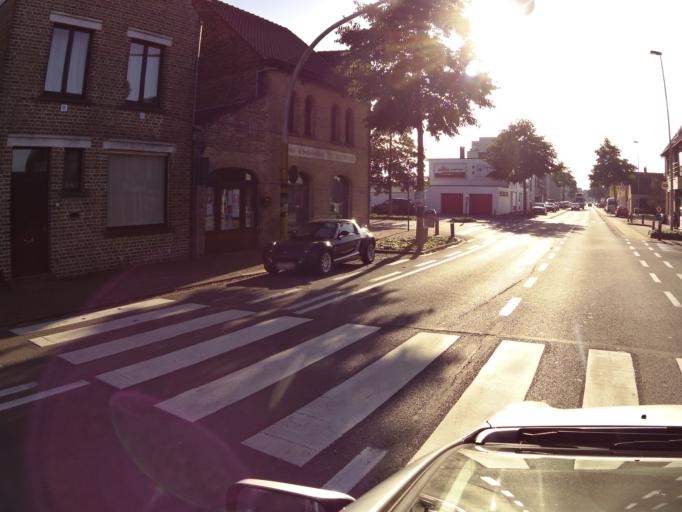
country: BE
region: Flanders
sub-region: Provincie West-Vlaanderen
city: Veurne
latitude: 51.0766
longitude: 2.6726
